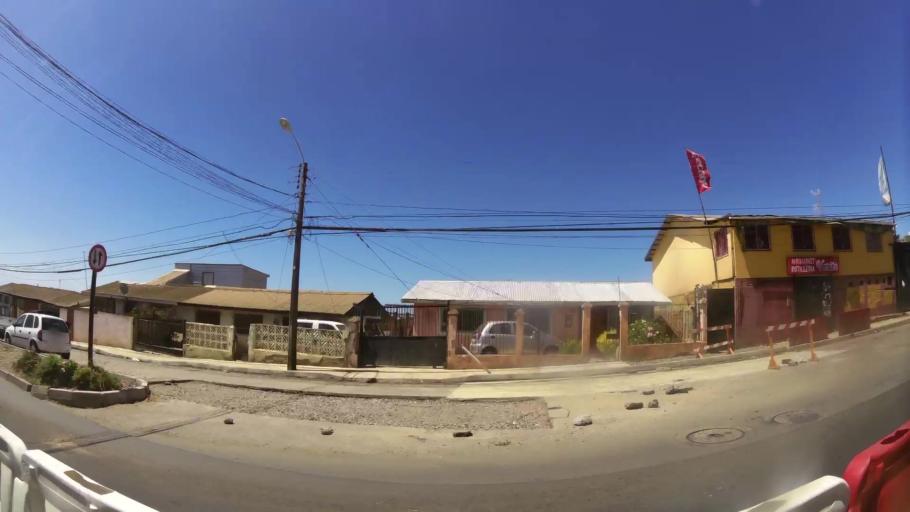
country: CL
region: Valparaiso
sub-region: Provincia de Valparaiso
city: Valparaiso
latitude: -33.0596
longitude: -71.6426
